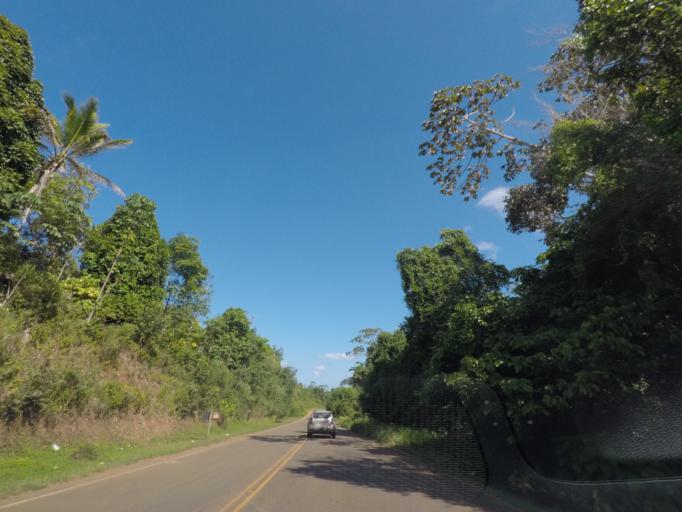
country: BR
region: Bahia
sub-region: Camamu
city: Camamu
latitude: -13.8955
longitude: -39.1381
